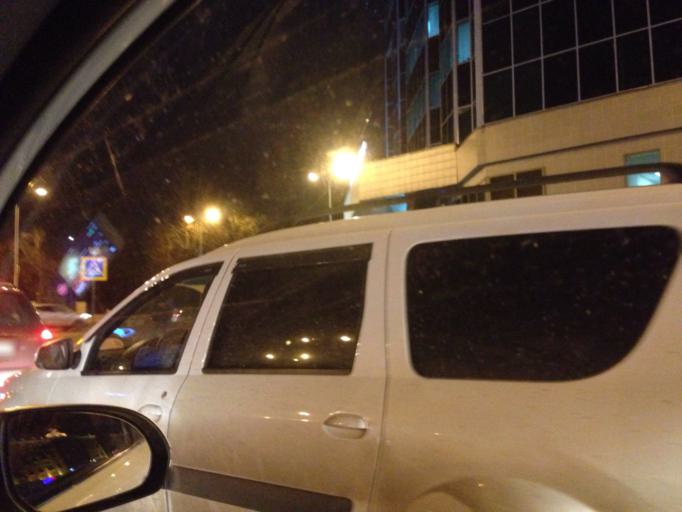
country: KZ
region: Astana Qalasy
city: Astana
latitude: 51.1681
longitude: 71.4267
